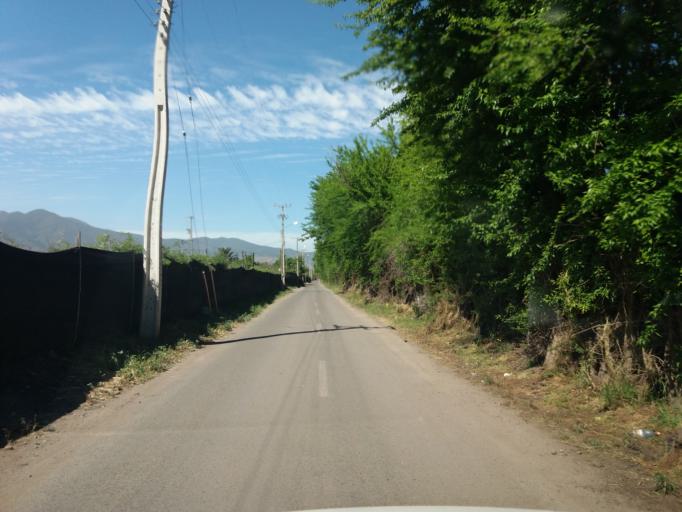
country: CL
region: Valparaiso
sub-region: Provincia de Quillota
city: Quillota
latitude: -32.8668
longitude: -71.2133
